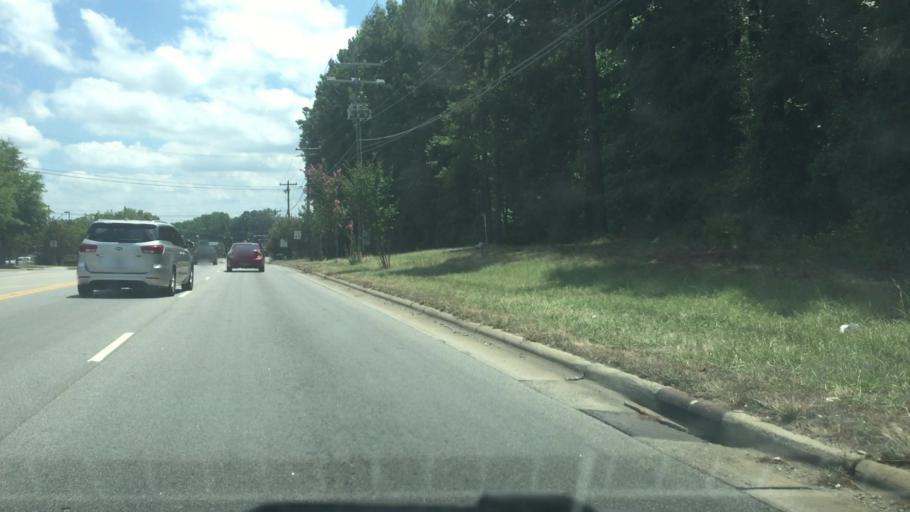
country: US
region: North Carolina
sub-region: Rowan County
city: Salisbury
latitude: 35.6683
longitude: -80.4996
